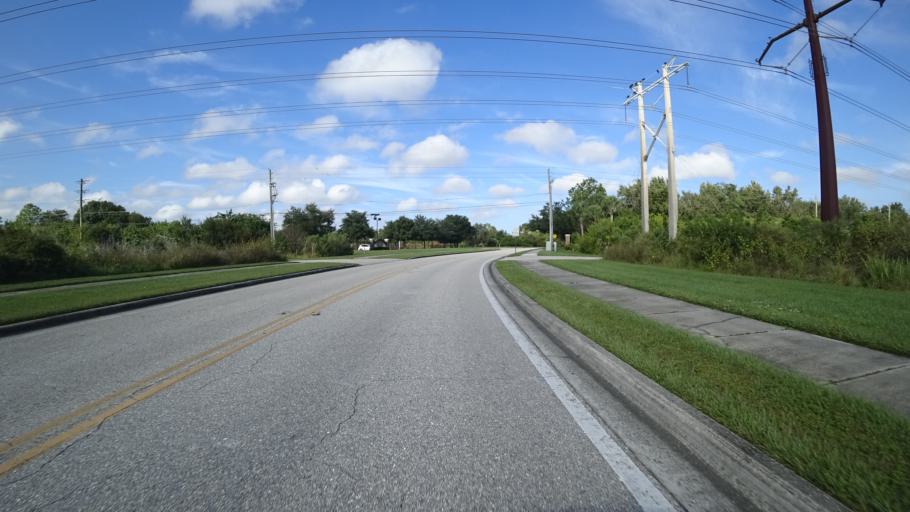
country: US
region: Florida
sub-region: Sarasota County
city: The Meadows
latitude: 27.3976
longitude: -82.4549
